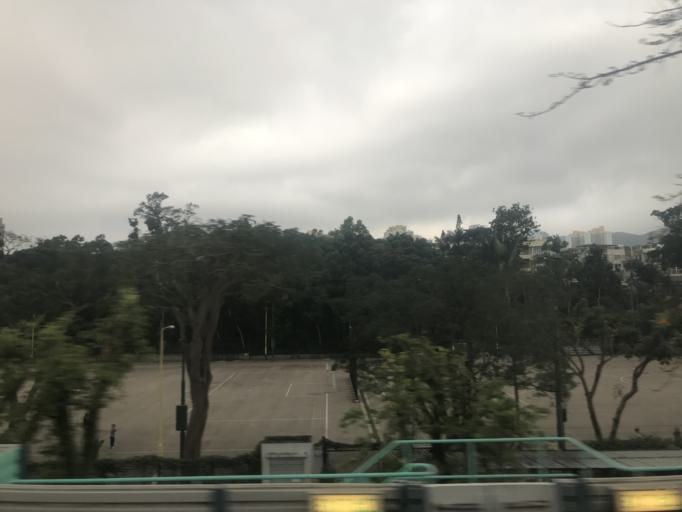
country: HK
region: Kowloon City
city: Kowloon
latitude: 22.3280
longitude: 114.1752
